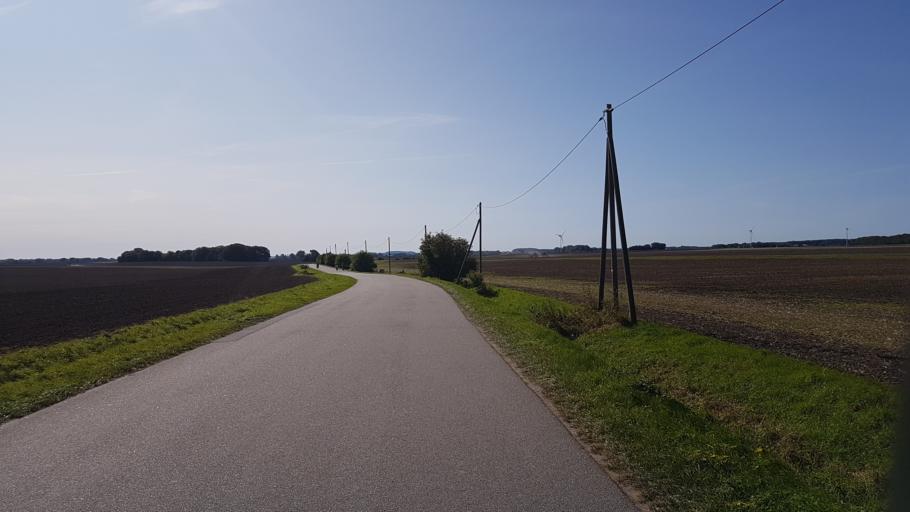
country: DE
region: Mecklenburg-Vorpommern
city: Altenkirchen
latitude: 54.6631
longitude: 13.3517
